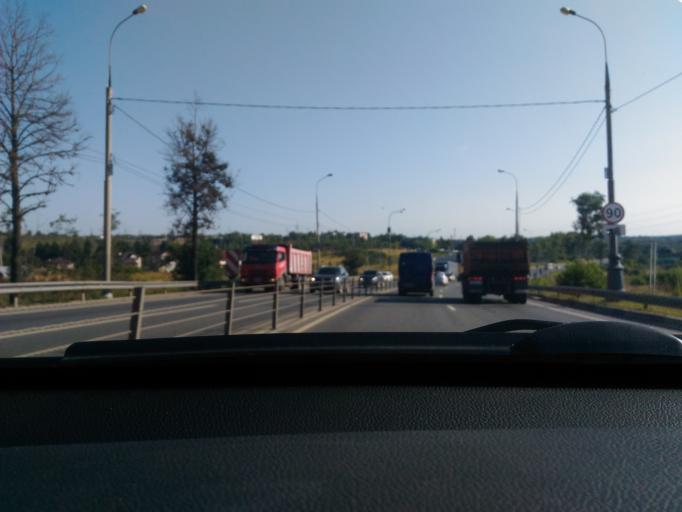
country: RU
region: Moskovskaya
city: Yermolino
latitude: 56.1590
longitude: 37.4887
